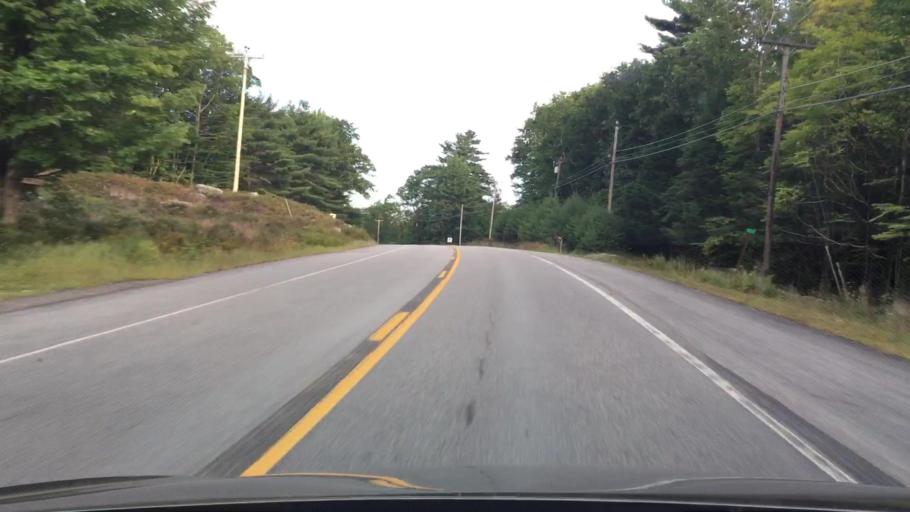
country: US
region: Maine
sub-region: Cumberland County
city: Bridgton
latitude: 44.0663
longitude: -70.7586
